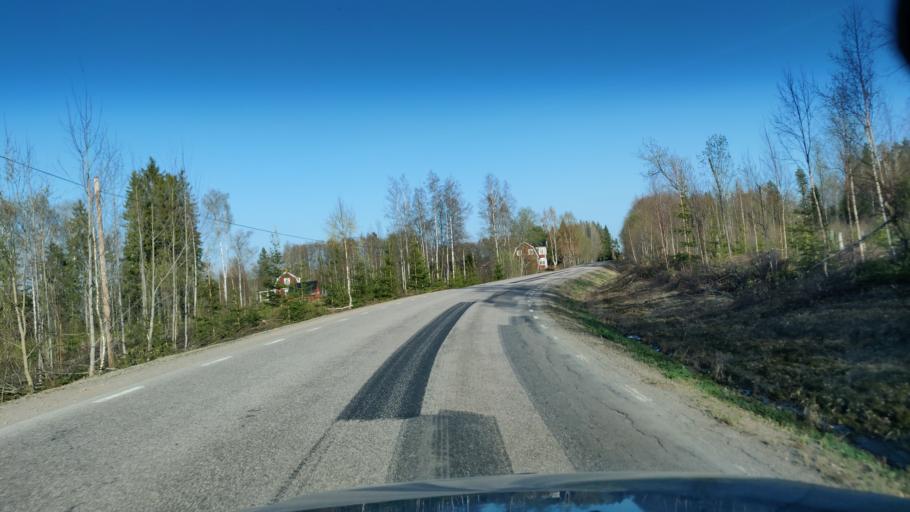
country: SE
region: Vaermland
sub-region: Munkfors Kommun
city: Munkfors
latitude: 59.9707
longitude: 13.4534
